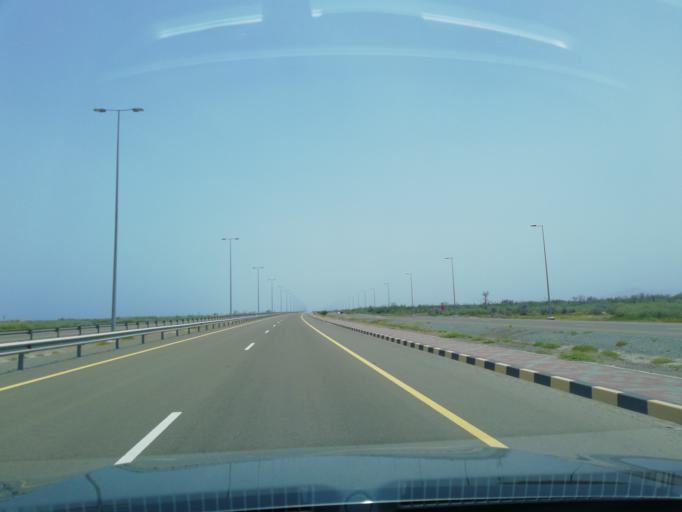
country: OM
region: Al Batinah
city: Shinas
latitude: 24.8901
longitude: 56.4012
